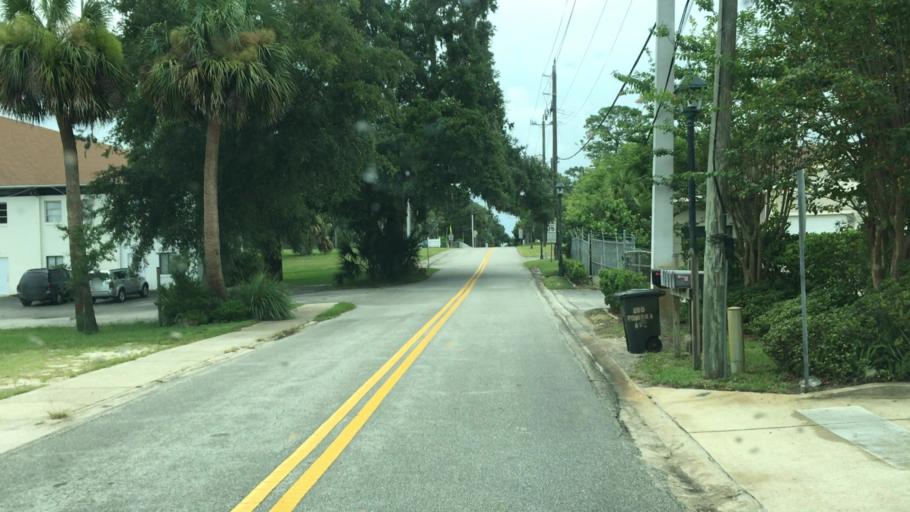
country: US
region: Florida
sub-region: Volusia County
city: Ormond Beach
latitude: 29.2822
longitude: -81.0591
